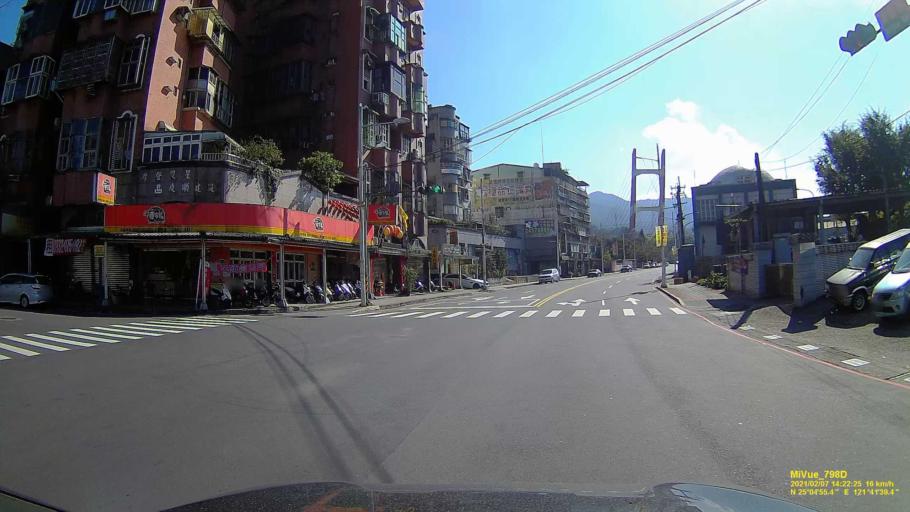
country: TW
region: Taiwan
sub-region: Keelung
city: Keelung
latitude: 25.0819
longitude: 121.6943
